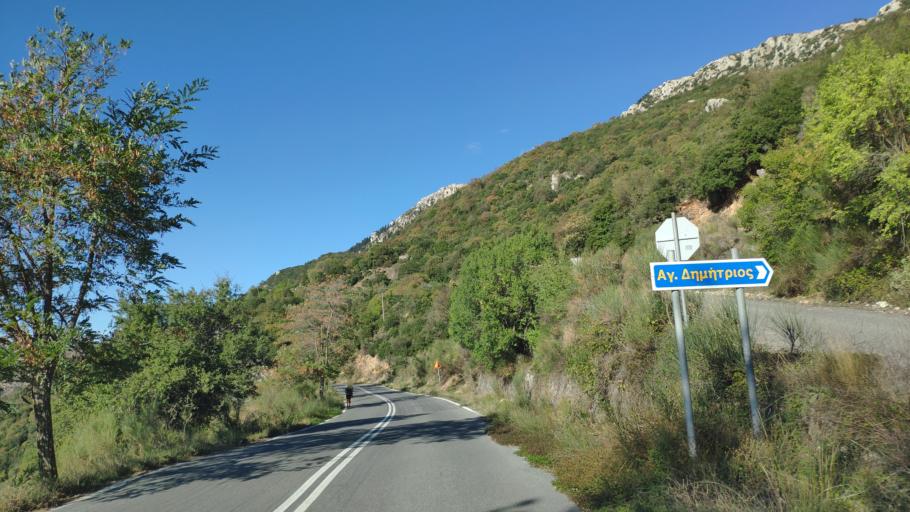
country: GR
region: Peloponnese
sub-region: Nomos Arkadias
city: Dimitsana
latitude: 37.5565
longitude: 22.0632
